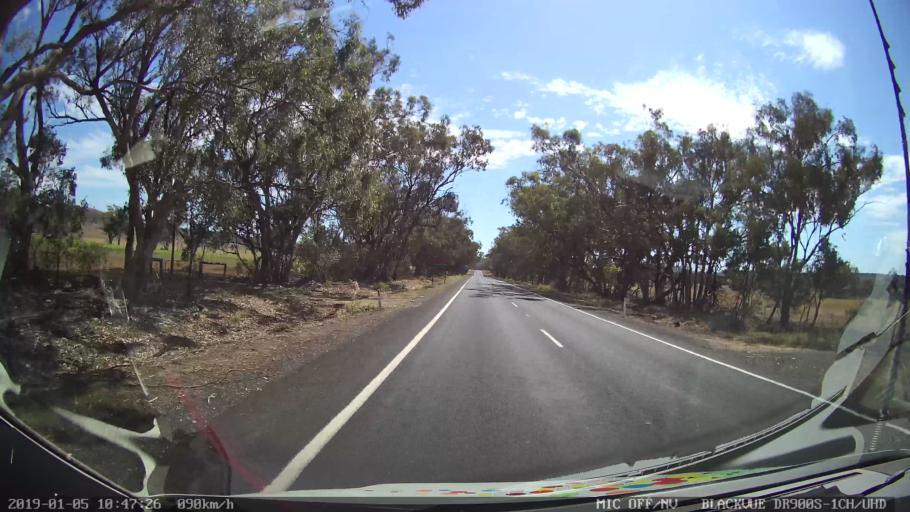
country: AU
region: New South Wales
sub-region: Warrumbungle Shire
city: Coonabarabran
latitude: -31.4450
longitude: 149.0329
